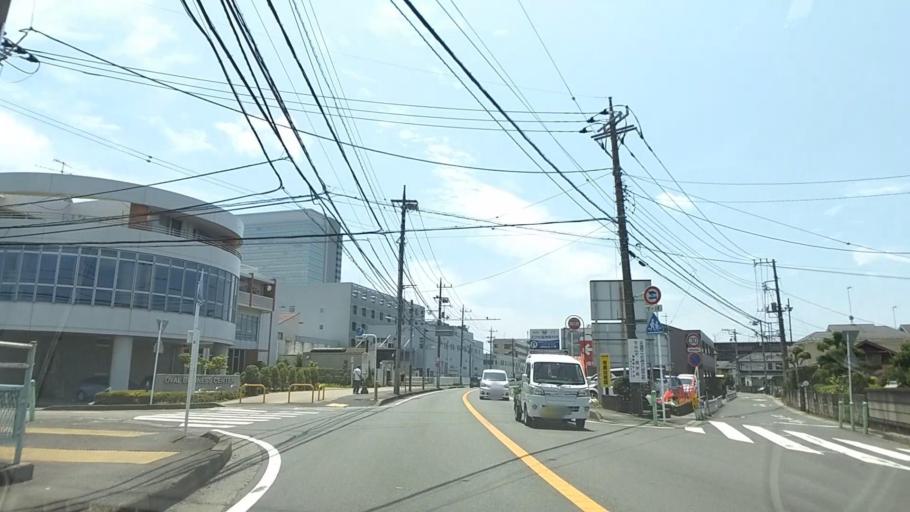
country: JP
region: Kanagawa
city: Zama
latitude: 35.4627
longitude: 139.3884
